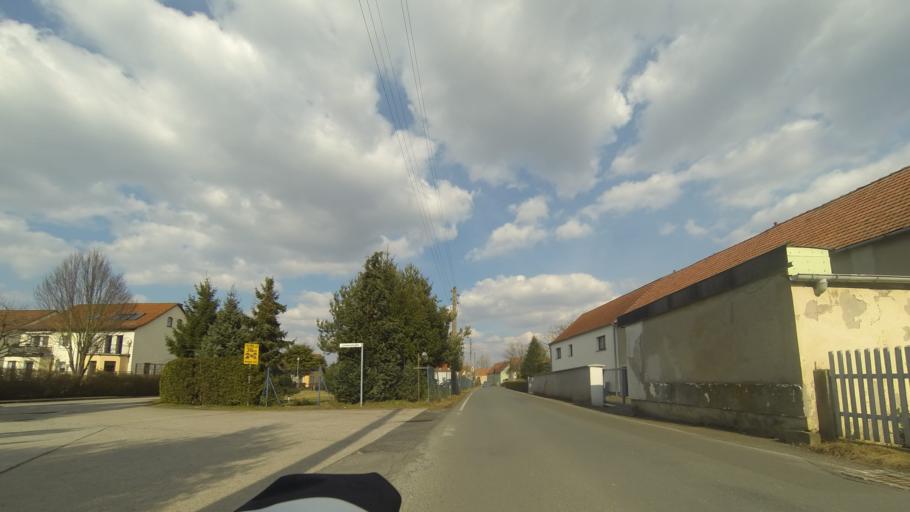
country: DE
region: Saxony
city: Ebersbach
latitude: 51.2591
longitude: 13.6763
